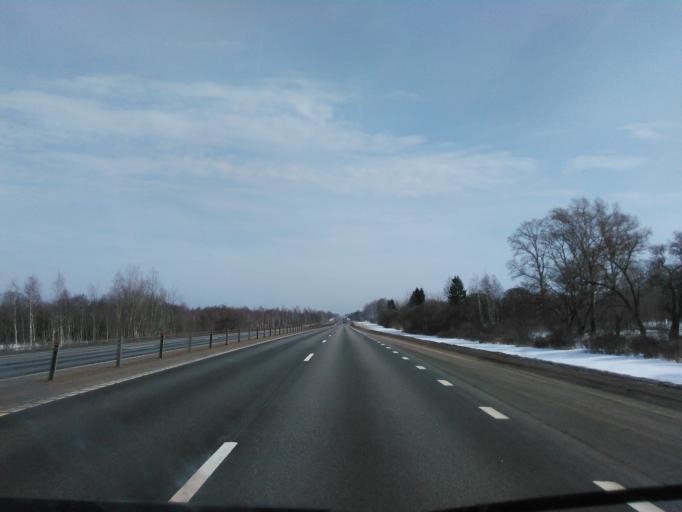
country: BY
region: Vitebsk
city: Dubrowna
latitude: 54.6894
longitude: 30.8955
